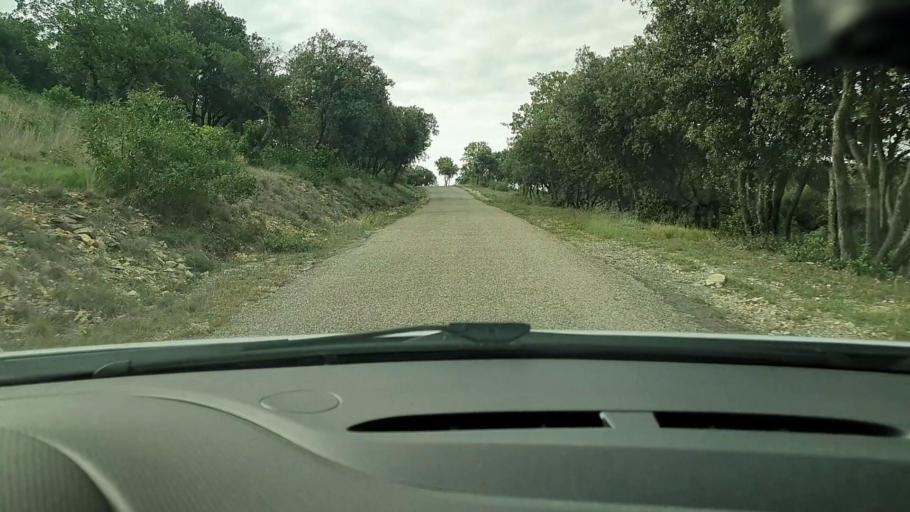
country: FR
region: Languedoc-Roussillon
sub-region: Departement du Gard
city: Montaren-et-Saint-Mediers
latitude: 44.0968
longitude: 4.3191
